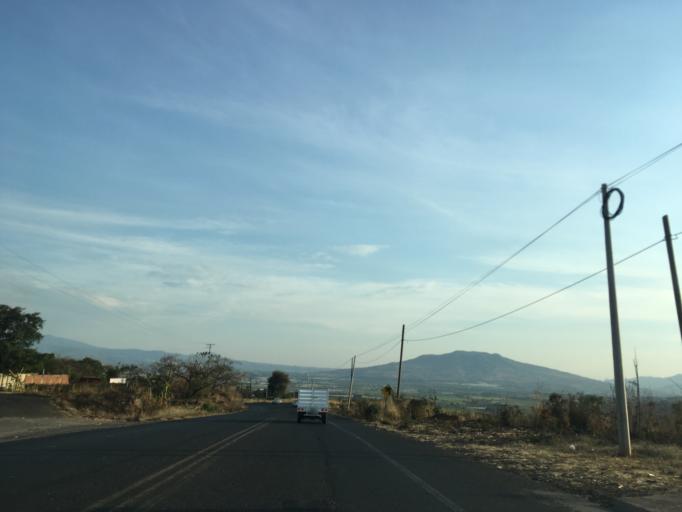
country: MX
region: Michoacan
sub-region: Los Reyes
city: La Higuerita (Colonia San Rafael)
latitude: 19.6583
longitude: -102.4938
